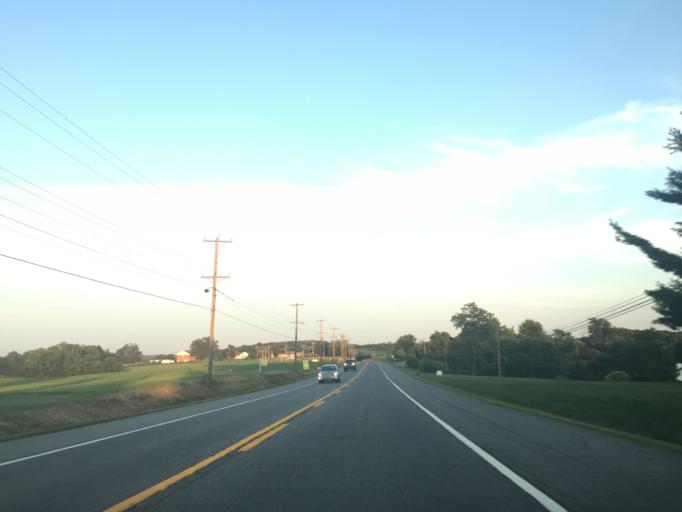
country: US
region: Pennsylvania
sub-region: York County
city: Susquehanna Trails
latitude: 39.6932
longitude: -76.3094
